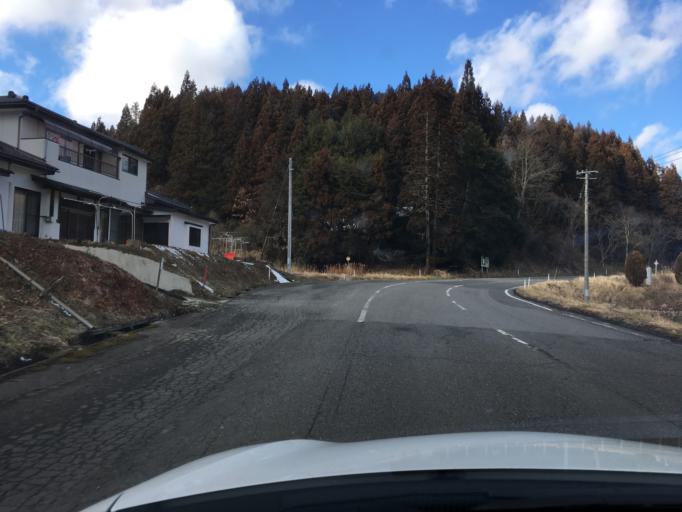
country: JP
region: Fukushima
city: Funehikimachi-funehiki
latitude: 37.2717
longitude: 140.5822
